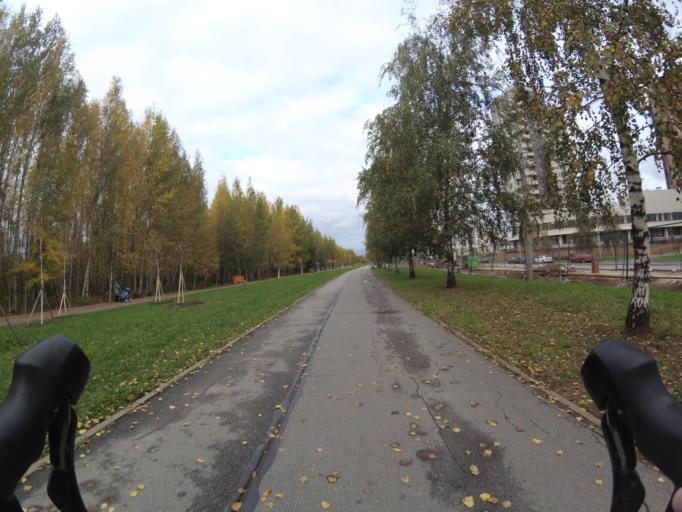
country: RU
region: Leningrad
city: Untolovo
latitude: 59.9993
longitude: 30.1930
